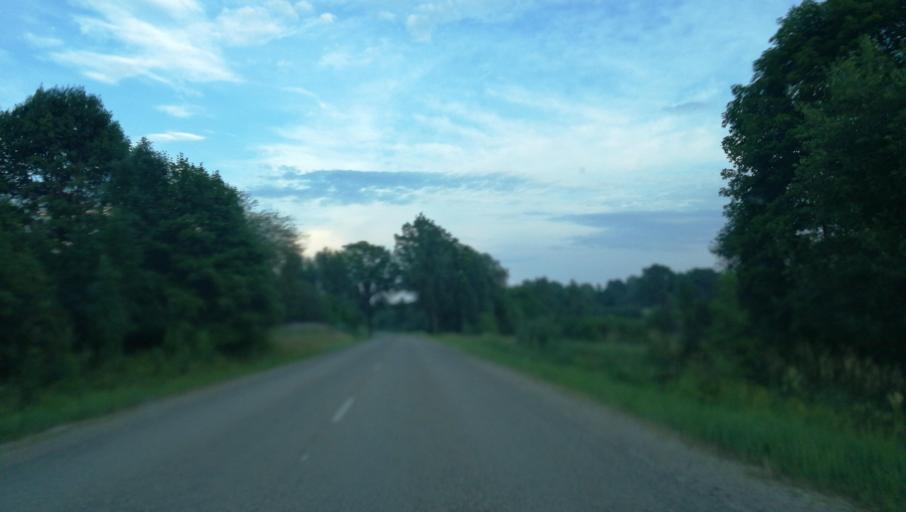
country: LV
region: Priekuli
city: Priekuli
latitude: 57.2630
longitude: 25.3561
